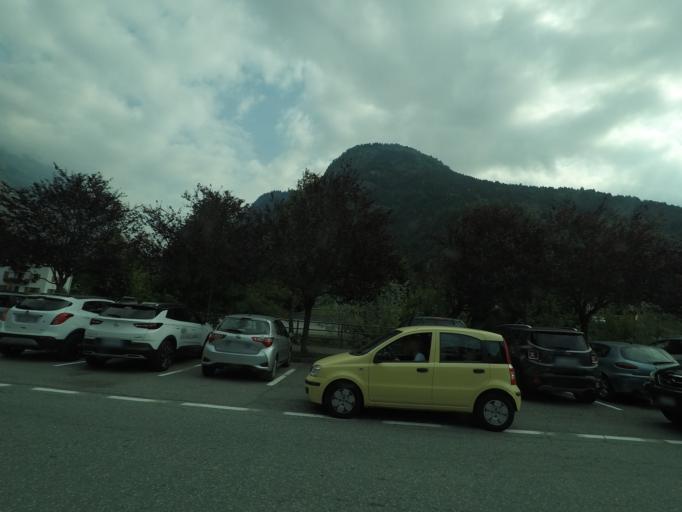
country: IT
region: Aosta Valley
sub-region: Valle d'Aosta
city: Antey-Saint-Andre
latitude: 45.8066
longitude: 7.5871
